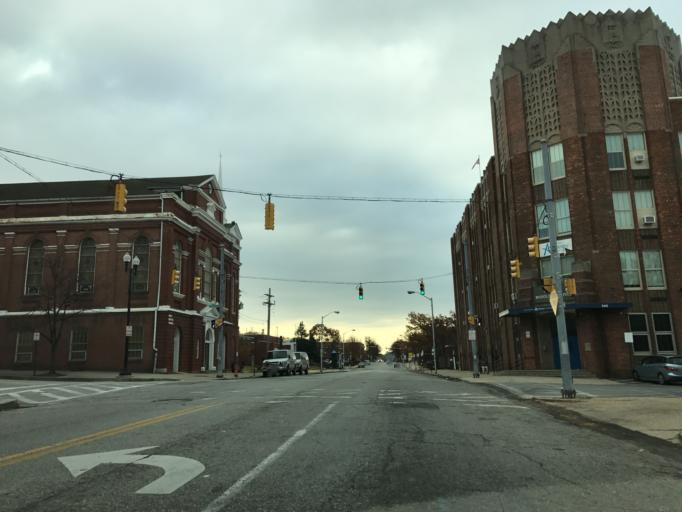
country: US
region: Maryland
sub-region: City of Baltimore
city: Baltimore
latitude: 39.2975
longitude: -76.5976
